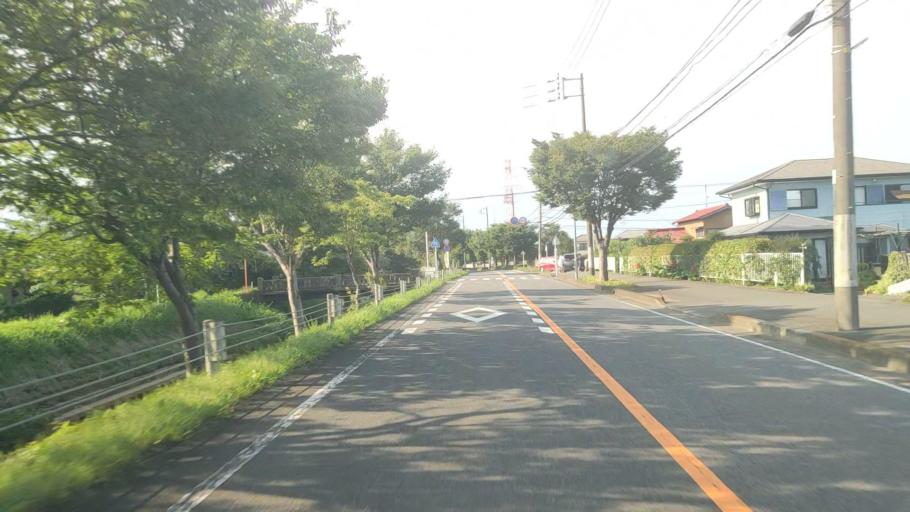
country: JP
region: Kanagawa
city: Isehara
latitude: 35.3947
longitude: 139.3379
